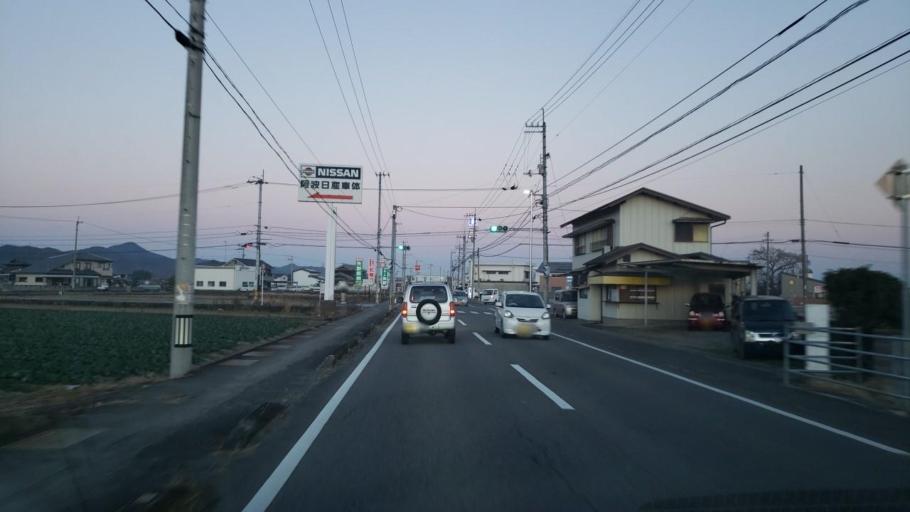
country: JP
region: Tokushima
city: Ishii
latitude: 34.1172
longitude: 134.4264
